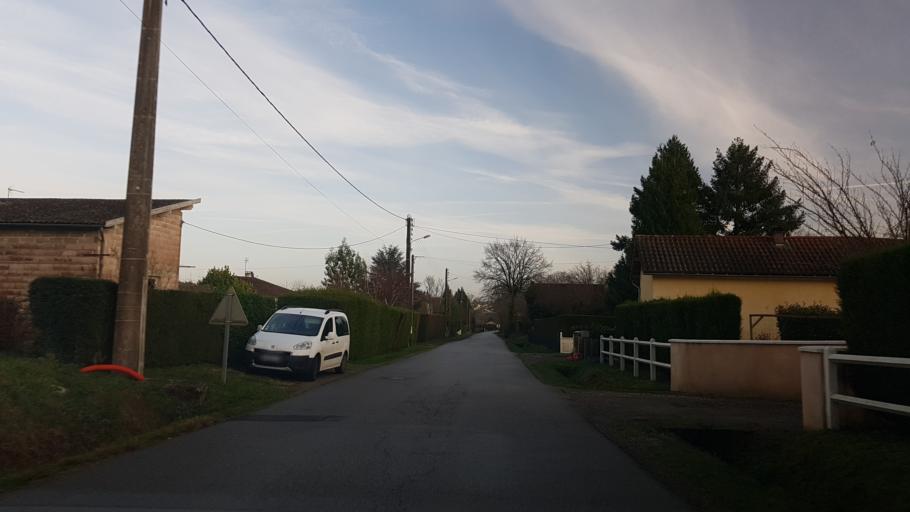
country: FR
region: Limousin
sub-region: Departement de la Haute-Vienne
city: Saint-Junien
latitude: 45.8961
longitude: 0.8693
